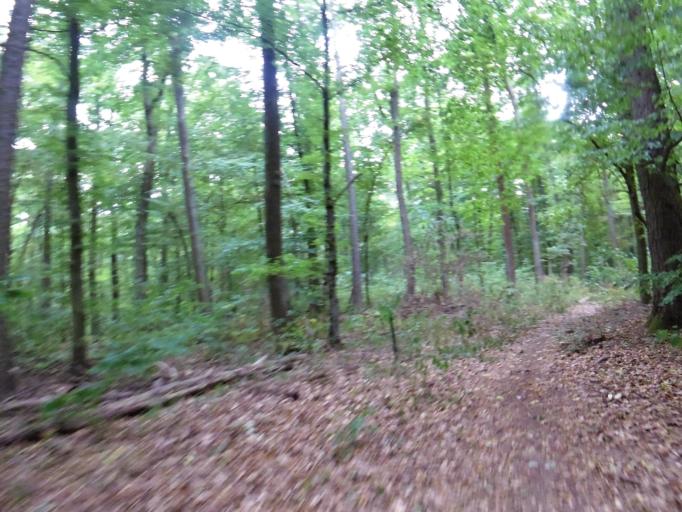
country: DE
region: Bavaria
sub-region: Regierungsbezirk Unterfranken
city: Waldbuttelbrunn
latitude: 49.7805
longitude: 9.8634
